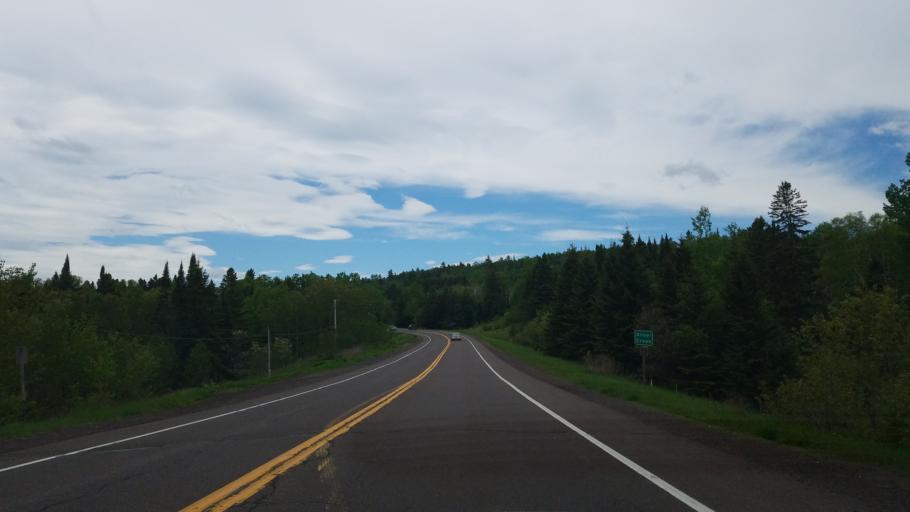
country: US
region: Minnesota
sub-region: Lake County
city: Two Harbors
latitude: 47.0645
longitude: -91.6043
